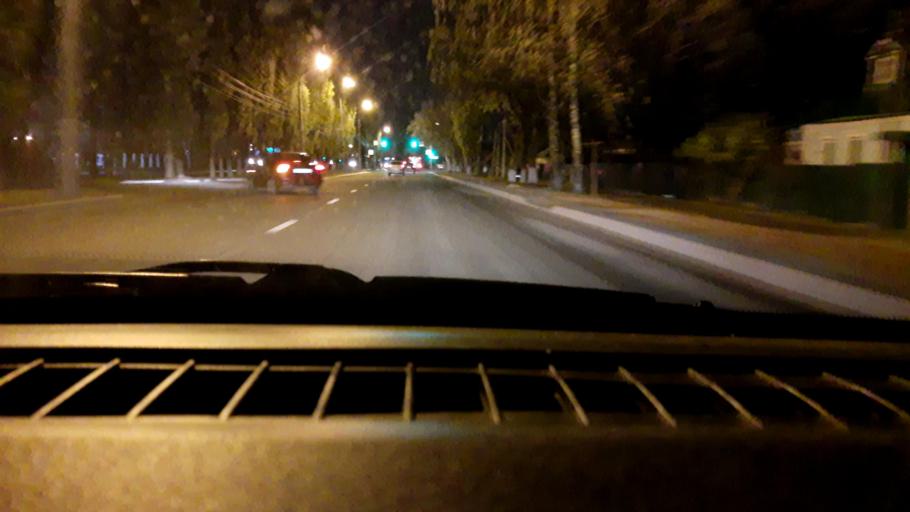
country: RU
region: Nizjnij Novgorod
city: Burevestnik
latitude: 56.2083
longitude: 43.8106
